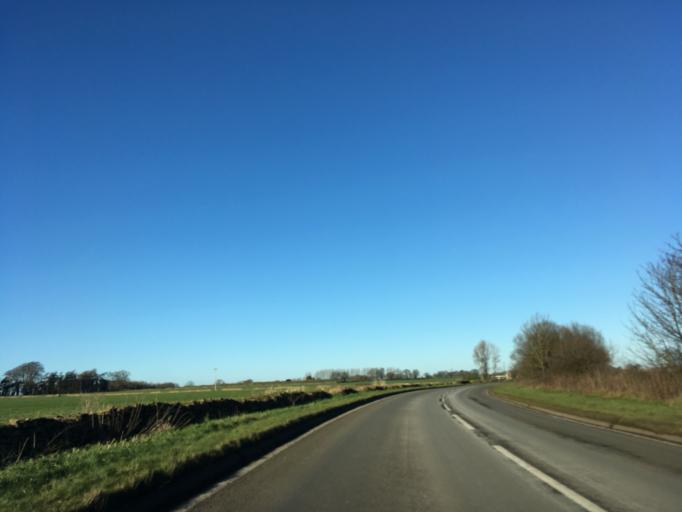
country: GB
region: England
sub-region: South Gloucestershire
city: Horton
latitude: 51.5339
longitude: -2.3438
